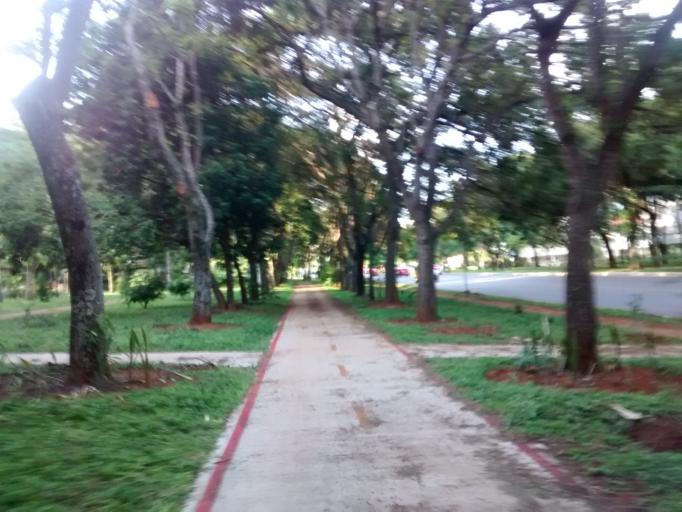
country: BR
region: Federal District
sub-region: Brasilia
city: Brasilia
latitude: -15.7820
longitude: -47.8772
